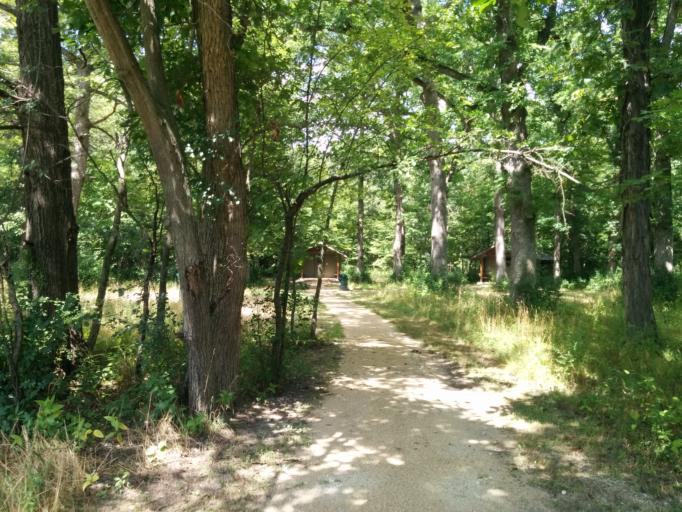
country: US
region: Illinois
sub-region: Lake County
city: Riverwoods
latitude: 42.1503
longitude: -87.8992
